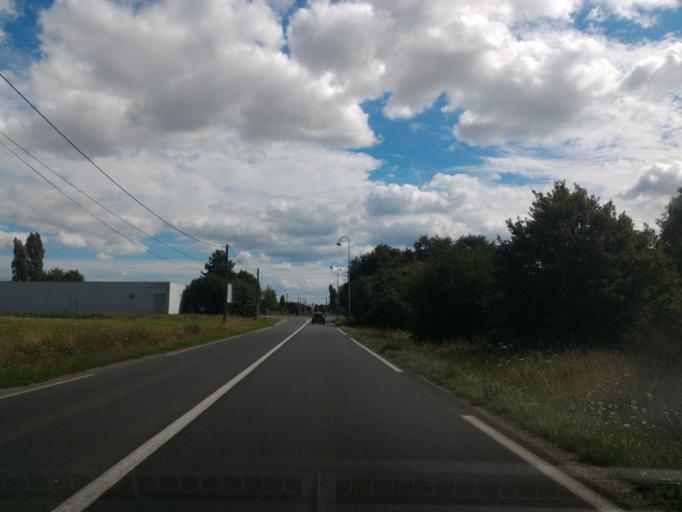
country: FR
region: Centre
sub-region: Departement d'Indre-et-Loire
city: Auzouer-en-Touraine
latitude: 47.5388
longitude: 0.9851
